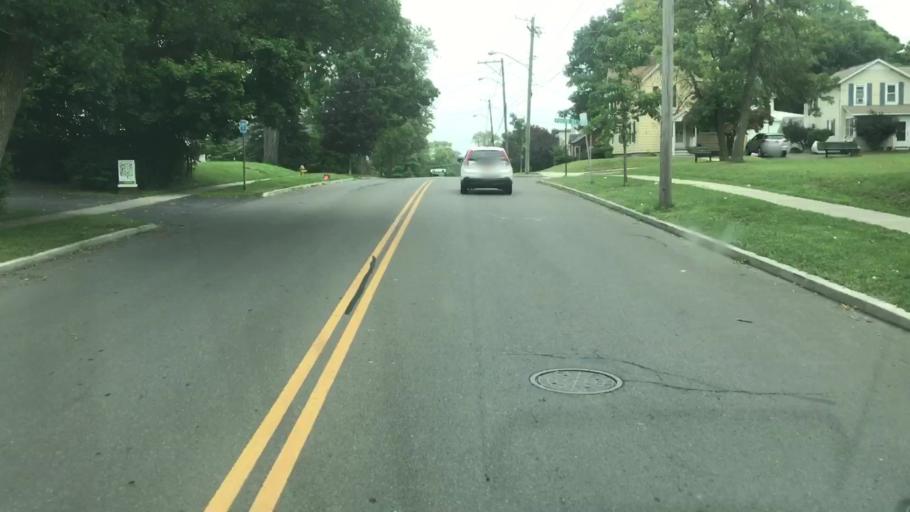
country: US
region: New York
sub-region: Cayuga County
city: Auburn
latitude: 42.9375
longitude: -76.5547
